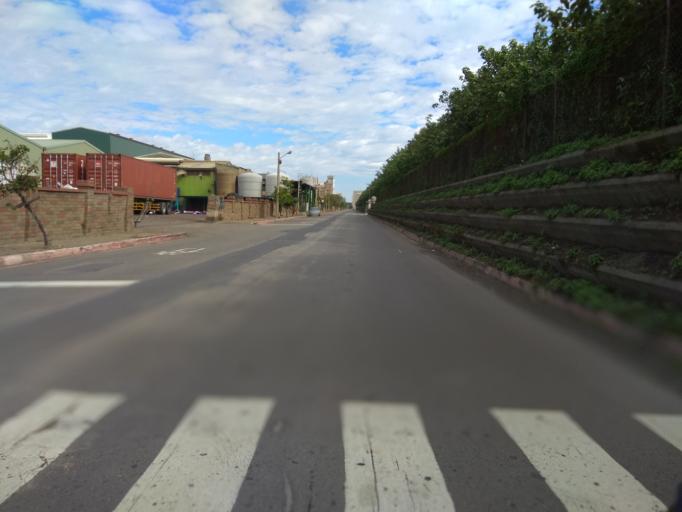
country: TW
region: Taiwan
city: Taoyuan City
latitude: 25.0577
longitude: 121.1059
